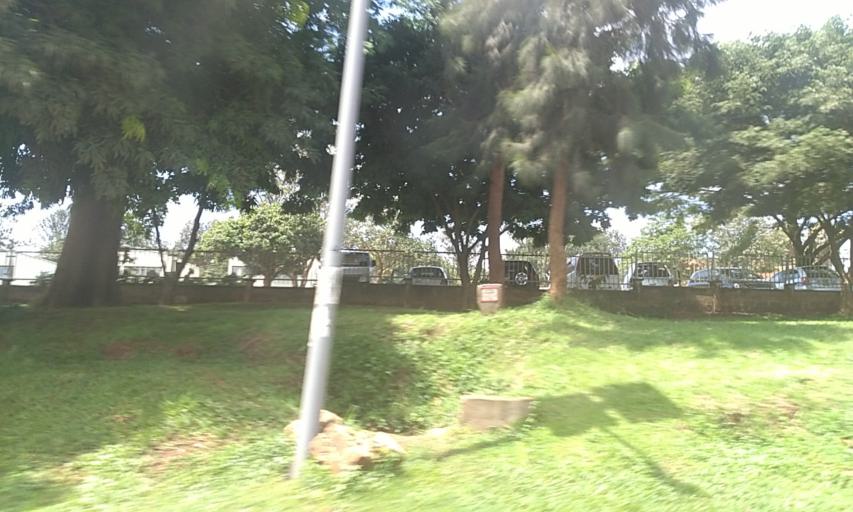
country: UG
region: Central Region
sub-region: Kampala District
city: Kampala
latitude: 0.3206
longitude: 32.5983
